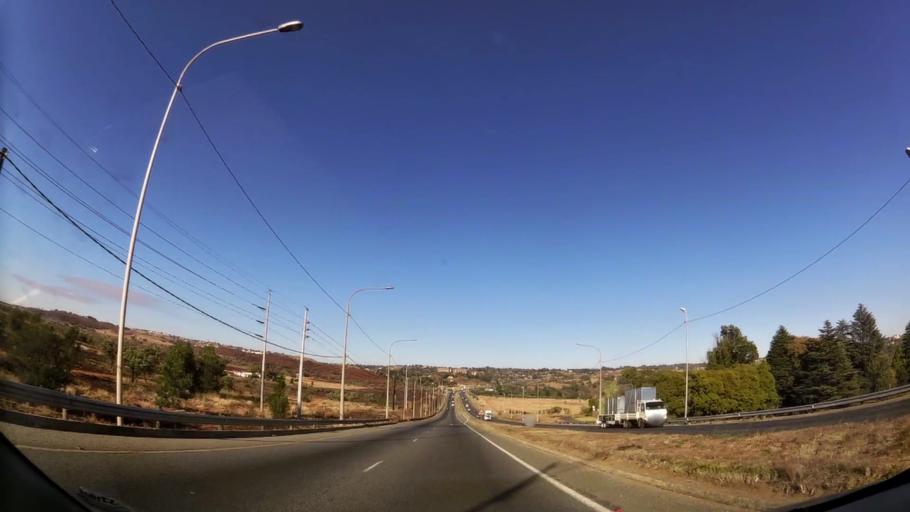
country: ZA
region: Gauteng
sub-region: West Rand District Municipality
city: Krugersdorp
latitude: -26.0660
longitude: 27.8053
